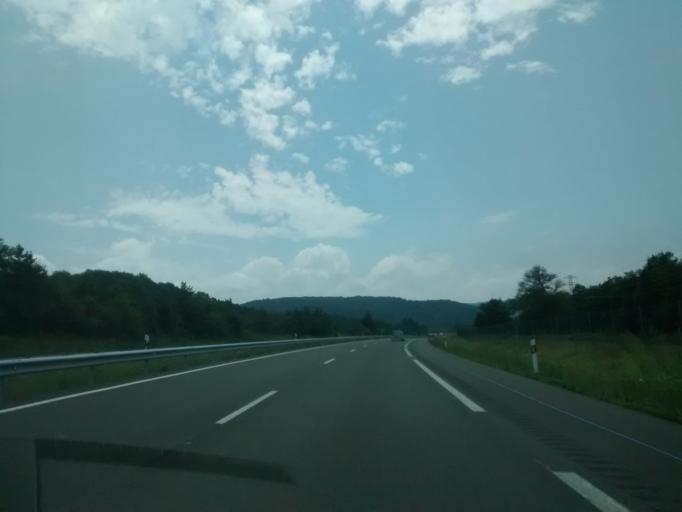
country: ES
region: Basque Country
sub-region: Provincia de Alava
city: Murguia
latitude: 42.9485
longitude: -2.8807
